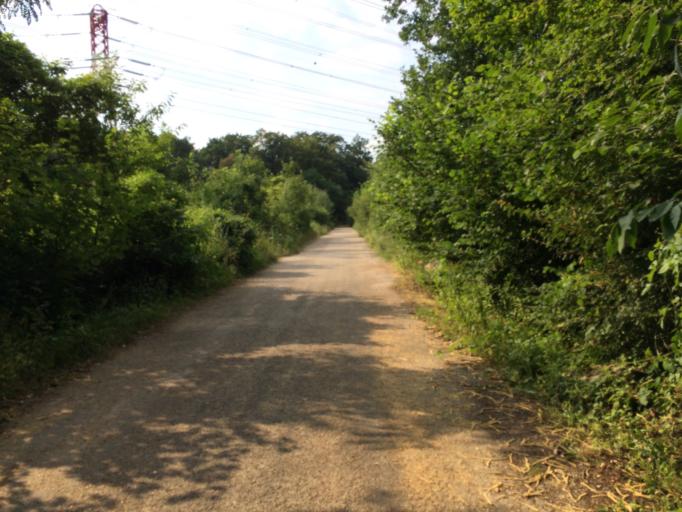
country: FR
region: Ile-de-France
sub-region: Departement de l'Essonne
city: Bievres
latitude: 48.7683
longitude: 2.2371
